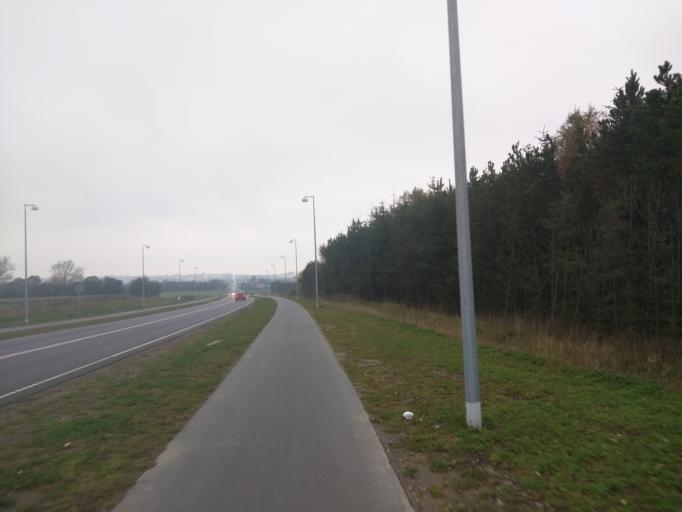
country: DK
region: Central Jutland
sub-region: Silkeborg Kommune
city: Silkeborg
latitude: 56.2051
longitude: 9.5111
